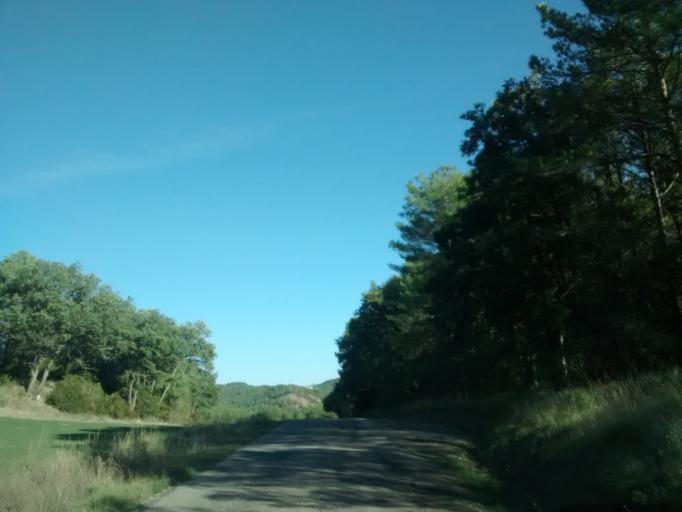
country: ES
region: Aragon
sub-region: Provincia de Huesca
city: Santa Cruz de la Seros
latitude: 42.4336
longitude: -0.6371
